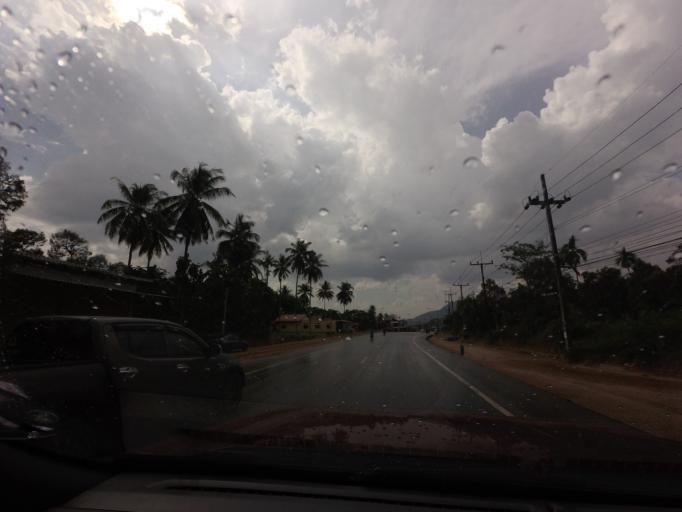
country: TH
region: Yala
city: Krong Pi Nang
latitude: 6.4100
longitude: 101.2800
